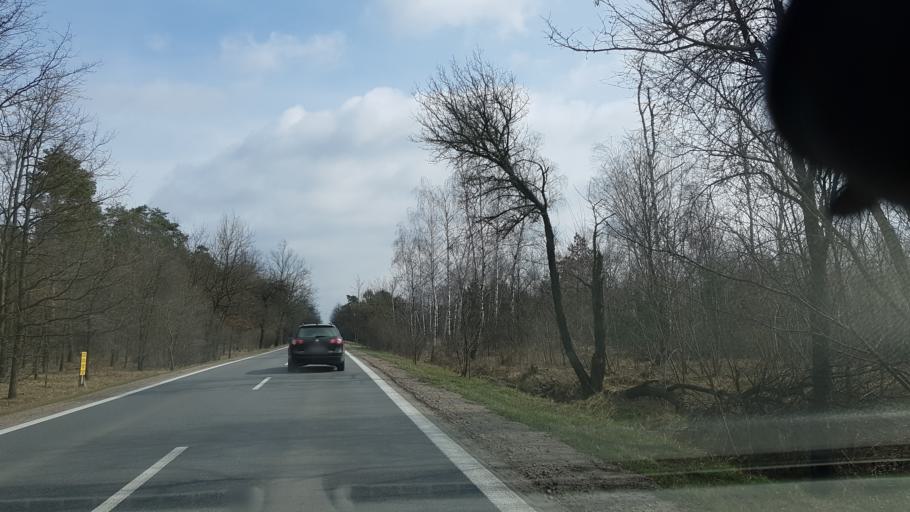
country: PL
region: Masovian Voivodeship
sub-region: Warszawa
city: Rembertow
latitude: 52.2564
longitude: 21.1846
